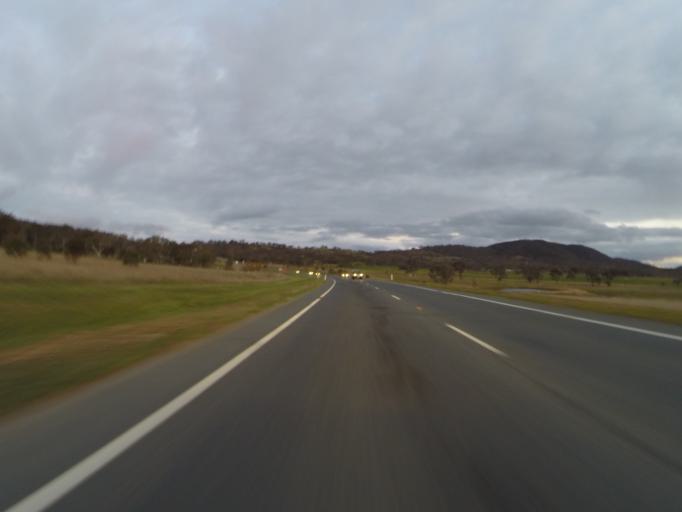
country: AU
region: Australian Capital Territory
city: Kaleen
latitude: -35.2097
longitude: 149.1725
